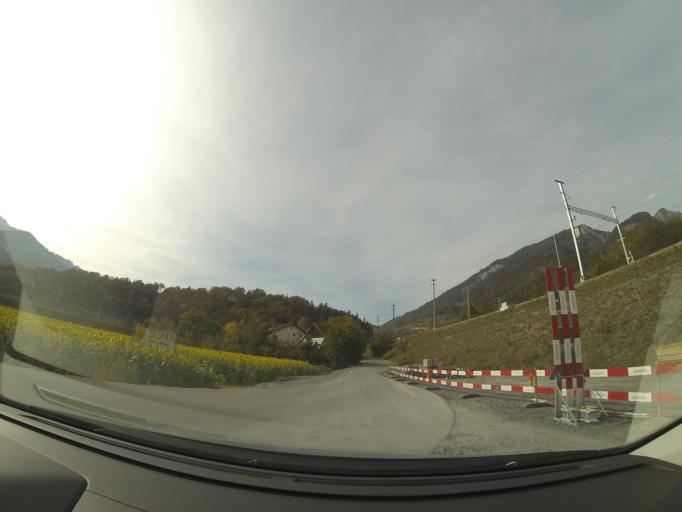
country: CH
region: Grisons
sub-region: Imboden District
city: Tamins
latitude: 46.8224
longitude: 9.4060
